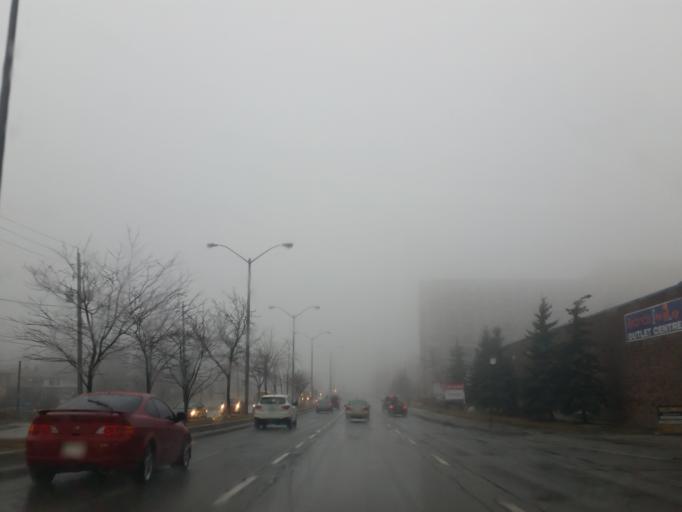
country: CA
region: Ontario
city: Scarborough
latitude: 43.7433
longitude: -79.2123
